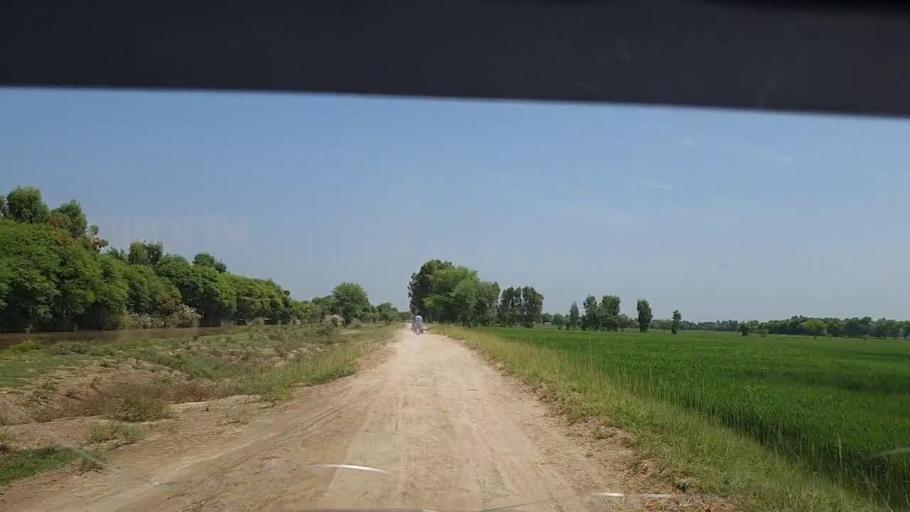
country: PK
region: Sindh
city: Tangwani
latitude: 28.2327
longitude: 68.9525
